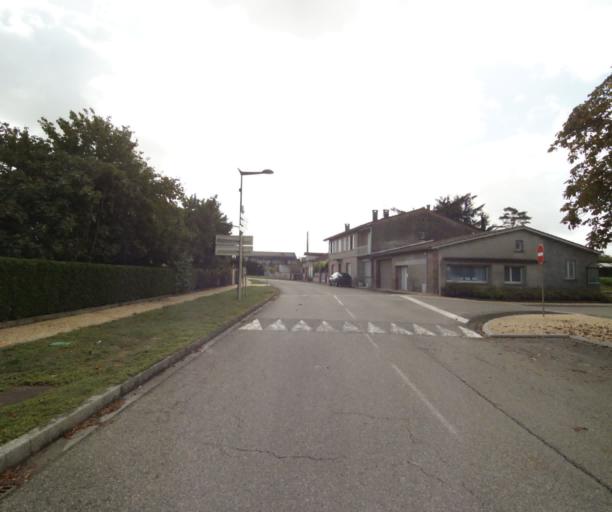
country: FR
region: Midi-Pyrenees
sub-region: Departement du Tarn-et-Garonne
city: Finhan
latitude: 43.8994
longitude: 1.1333
